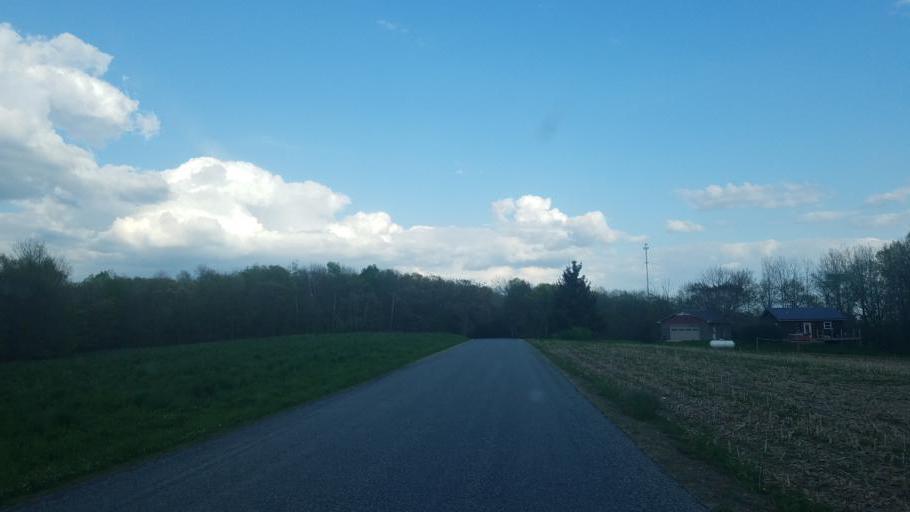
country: US
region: Wisconsin
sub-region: Vernon County
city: Hillsboro
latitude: 43.6744
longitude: -90.3600
